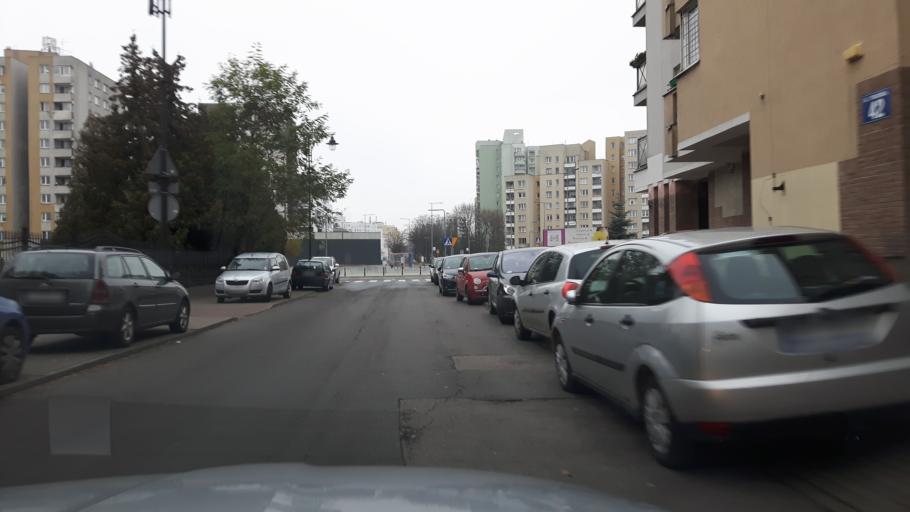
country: PL
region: Masovian Voivodeship
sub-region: Warszawa
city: Praga Polnoc
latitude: 52.2689
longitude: 21.0526
